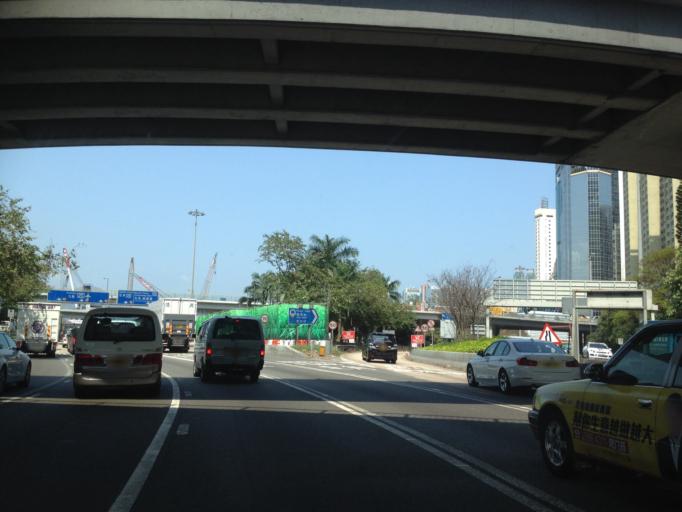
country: HK
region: Wanchai
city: Wan Chai
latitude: 22.2806
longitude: 114.1790
